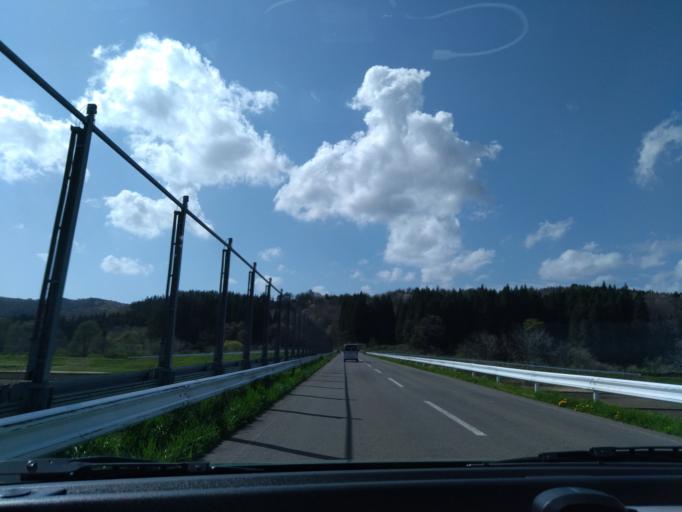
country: JP
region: Akita
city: Akita
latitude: 39.6946
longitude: 140.2708
